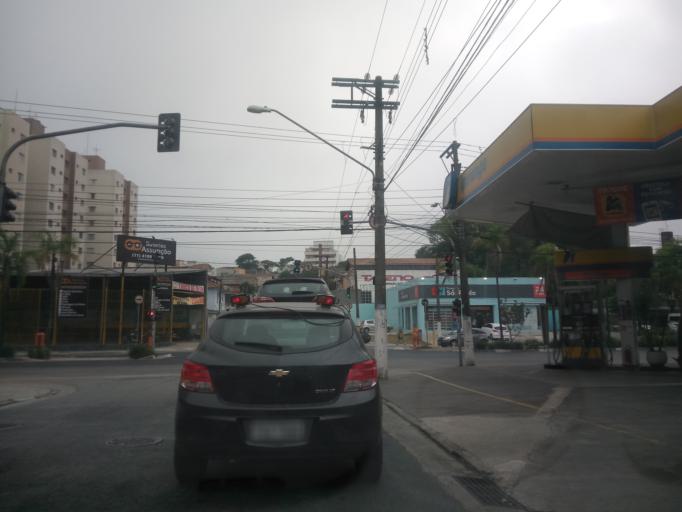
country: BR
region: Sao Paulo
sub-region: Sao Bernardo Do Campo
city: Sao Bernardo do Campo
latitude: -23.7223
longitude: -46.5675
